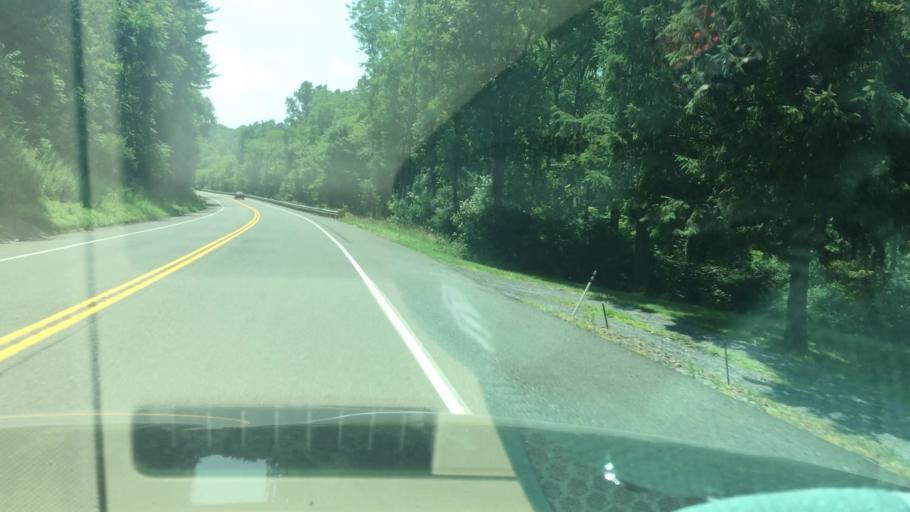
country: US
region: Pennsylvania
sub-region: Lehigh County
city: Schnecksville
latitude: 40.6650
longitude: -75.6873
